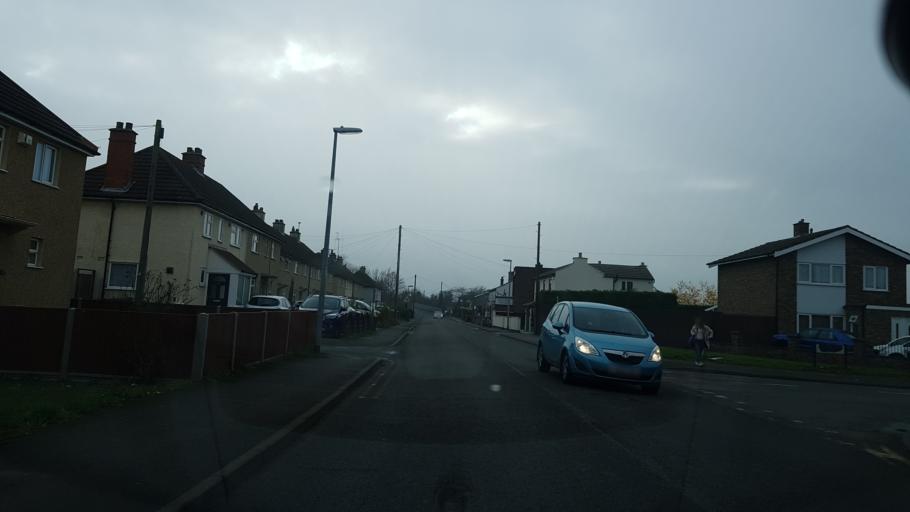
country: GB
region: England
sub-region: Central Bedfordshire
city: Biggleswade
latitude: 52.0929
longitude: -0.2579
